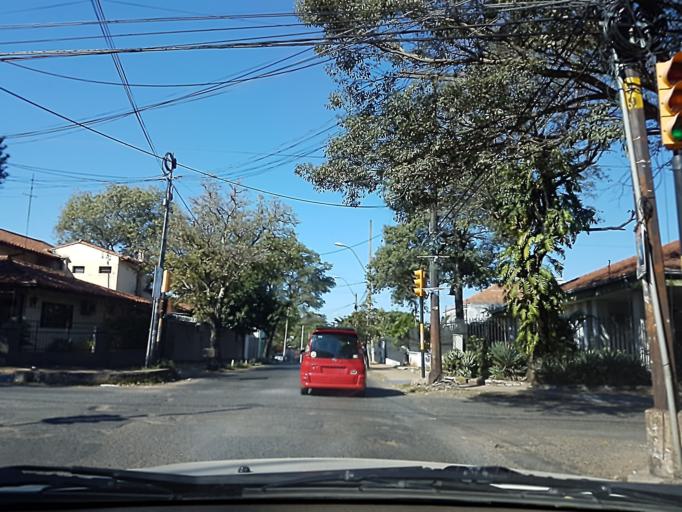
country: PY
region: Asuncion
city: Asuncion
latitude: -25.2969
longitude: -57.5875
